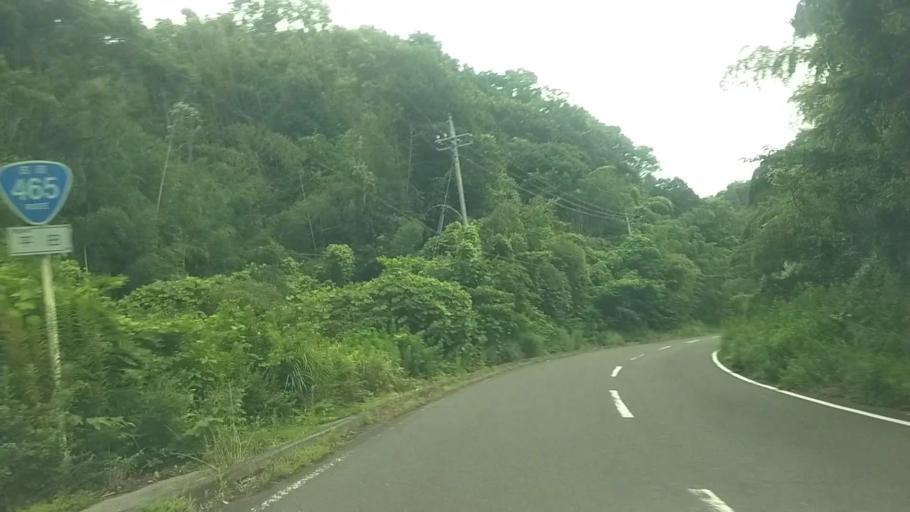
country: JP
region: Chiba
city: Kimitsu
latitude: 35.2386
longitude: 139.9791
